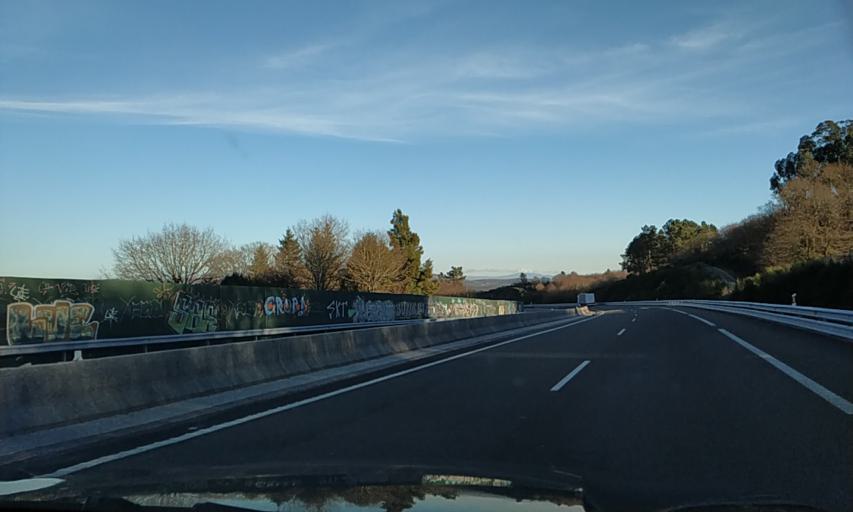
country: ES
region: Galicia
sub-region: Provincia de Pontevedra
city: Dozon
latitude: 42.5592
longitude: -8.0291
